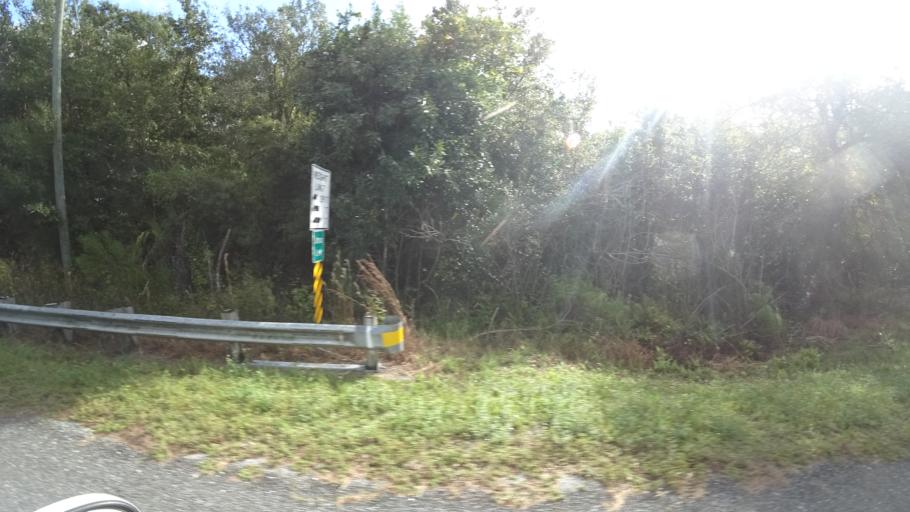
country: US
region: Florida
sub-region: Hillsborough County
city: Wimauma
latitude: 27.4620
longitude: -82.1531
